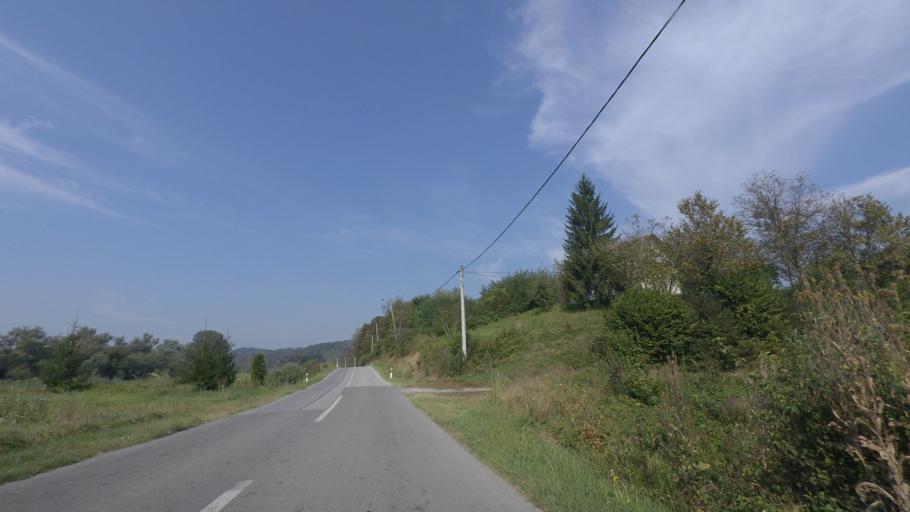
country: HR
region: Sisacko-Moslavacka
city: Hrvatska Kostajnica
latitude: 45.2322
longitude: 16.6013
